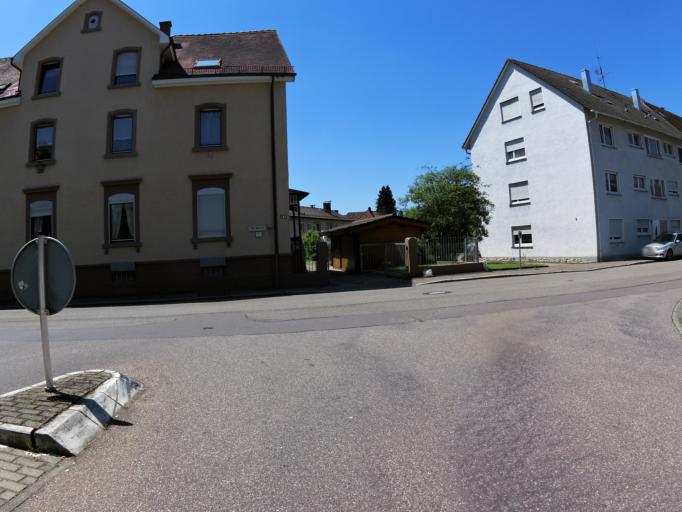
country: DE
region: Baden-Wuerttemberg
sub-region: Freiburg Region
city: Lahr
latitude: 48.3427
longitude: 7.8394
